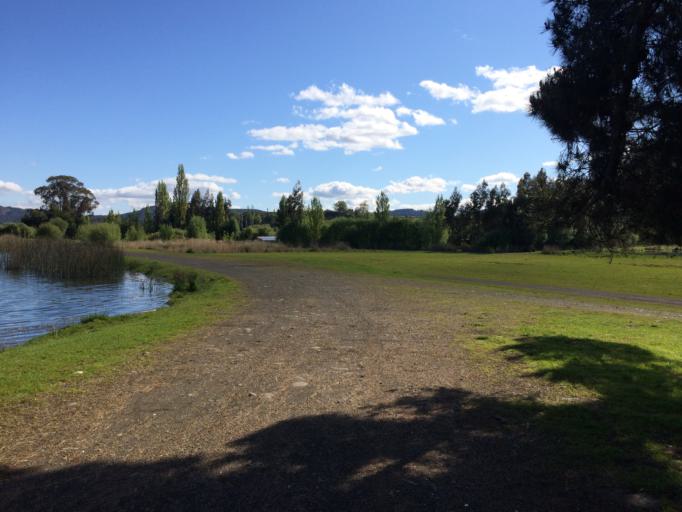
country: CL
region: Araucania
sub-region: Provincia de Cautin
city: Lautaro
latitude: -38.5490
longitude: -72.4304
